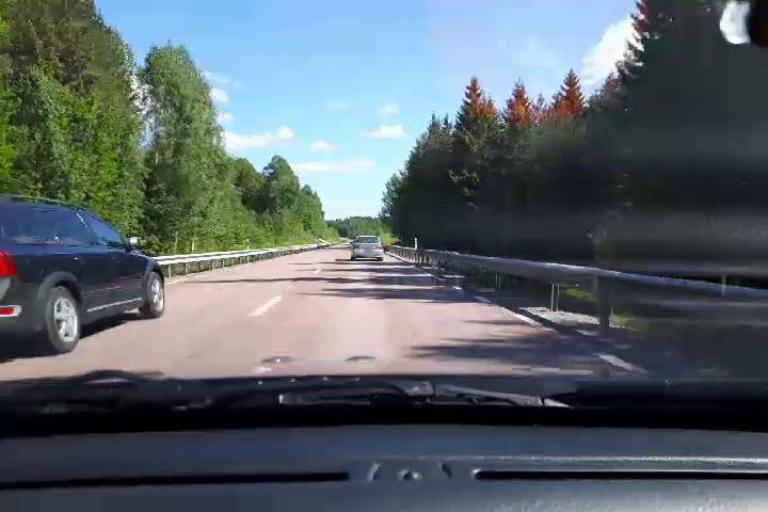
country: SE
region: Gaevleborg
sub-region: Hudiksvalls Kommun
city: Sorforsa
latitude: 61.7454
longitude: 16.8478
